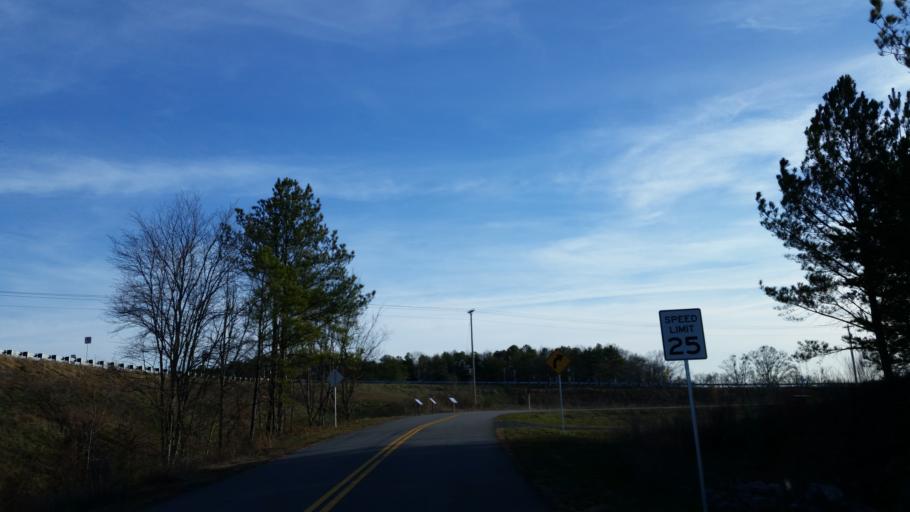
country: US
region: Georgia
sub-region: Gordon County
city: Calhoun
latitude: 34.5781
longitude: -84.9525
